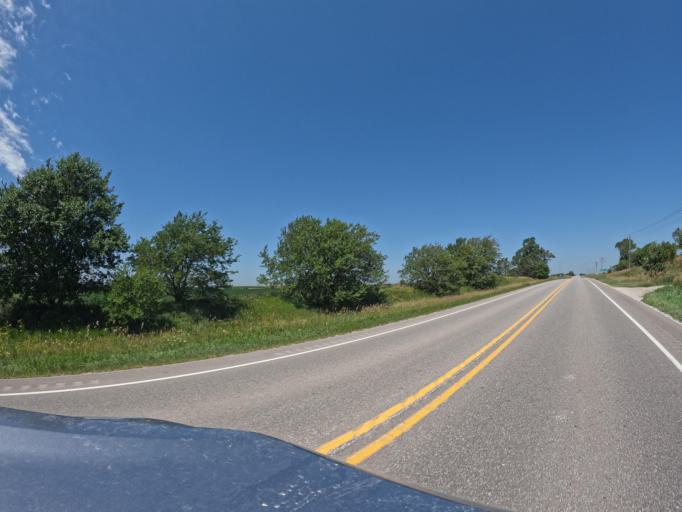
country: US
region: Iowa
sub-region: Keokuk County
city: Sigourney
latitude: 41.4502
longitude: -92.3551
